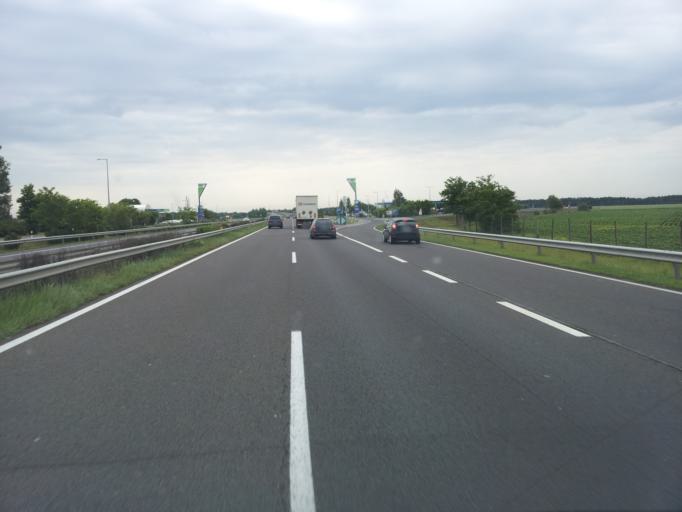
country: HU
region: Heves
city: Adacs
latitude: 47.7149
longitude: 20.0006
